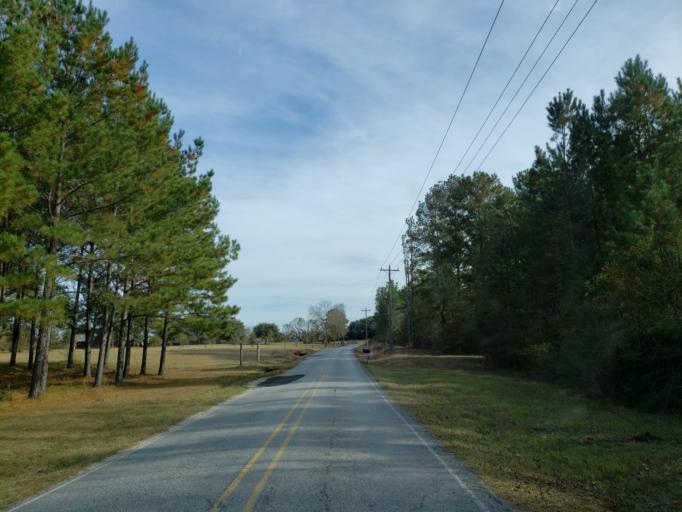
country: US
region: Mississippi
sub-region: Forrest County
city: Rawls Springs
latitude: 31.4122
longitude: -89.4114
